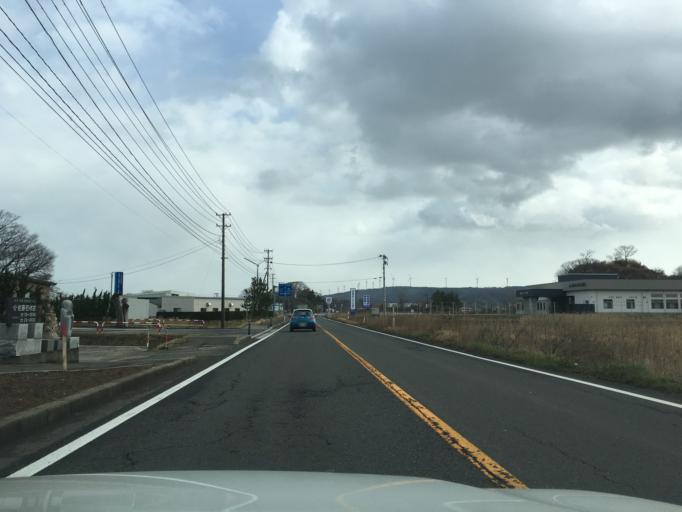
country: JP
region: Yamagata
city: Yuza
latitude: 39.2841
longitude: 139.9457
